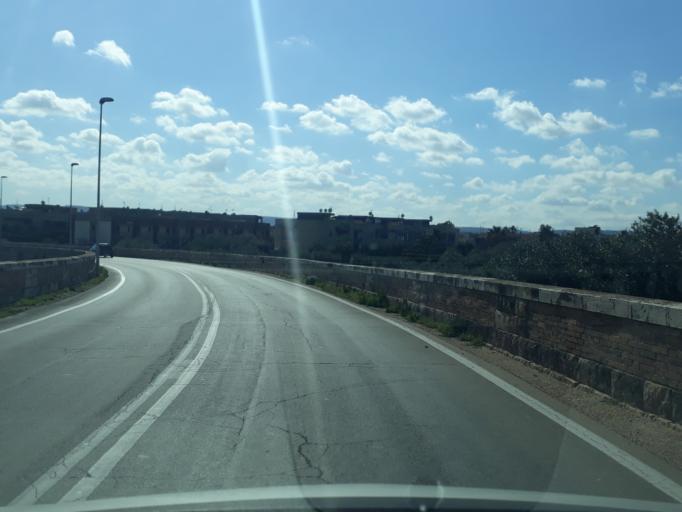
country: IT
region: Apulia
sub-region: Provincia di Bari
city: Monopoli
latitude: 40.9563
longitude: 17.2822
